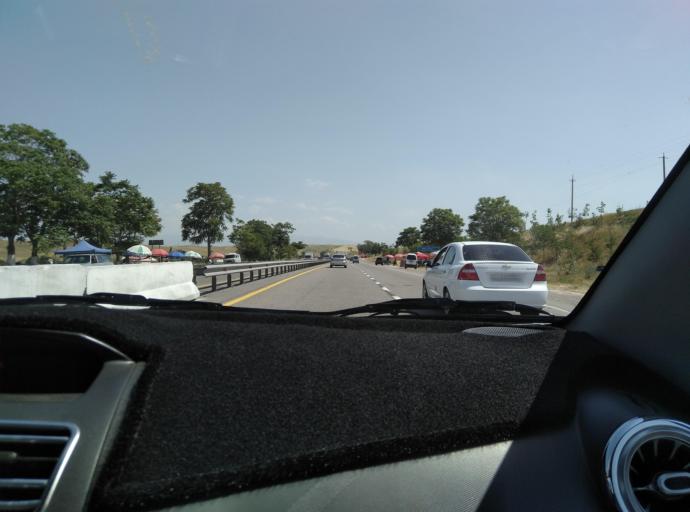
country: UZ
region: Toshkent
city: Ohangaron
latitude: 40.9789
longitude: 69.5416
